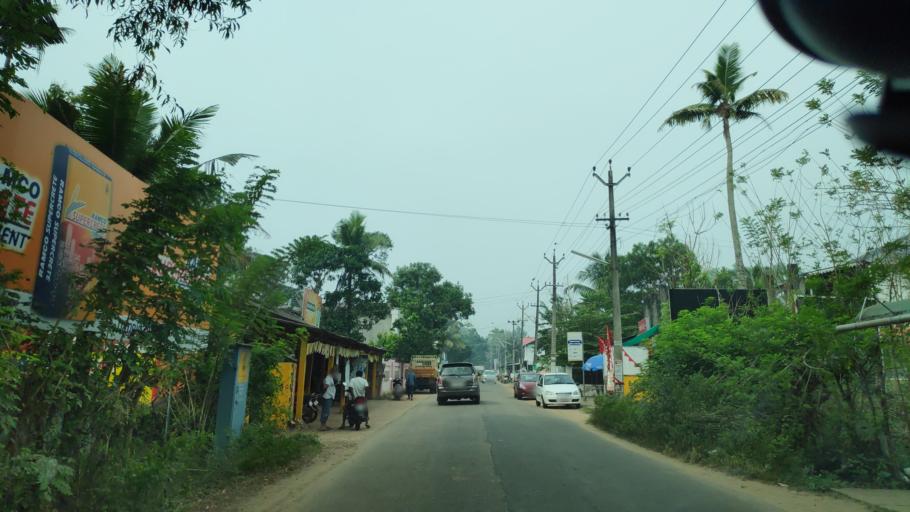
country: IN
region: Kerala
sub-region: Alappuzha
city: Alleppey
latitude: 9.5723
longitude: 76.3423
